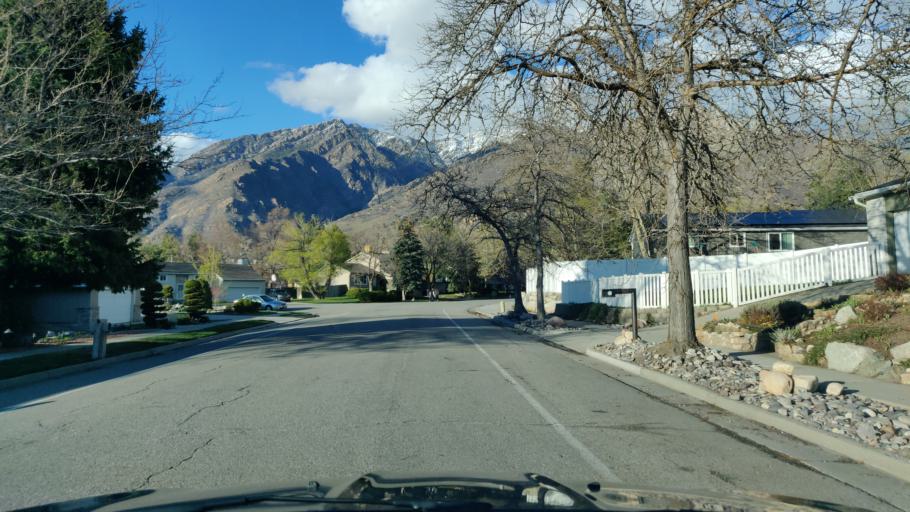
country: US
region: Utah
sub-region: Salt Lake County
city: Cottonwood Heights
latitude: 40.6186
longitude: -111.8034
